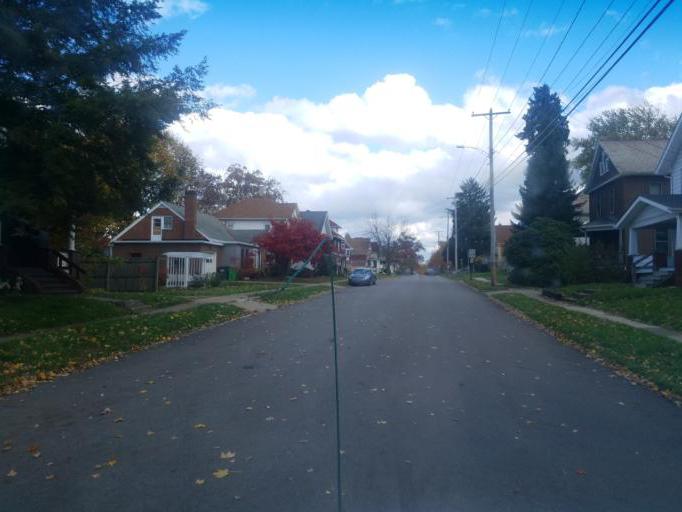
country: US
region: Ohio
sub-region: Wayne County
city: Orrville
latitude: 40.8346
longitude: -81.7697
